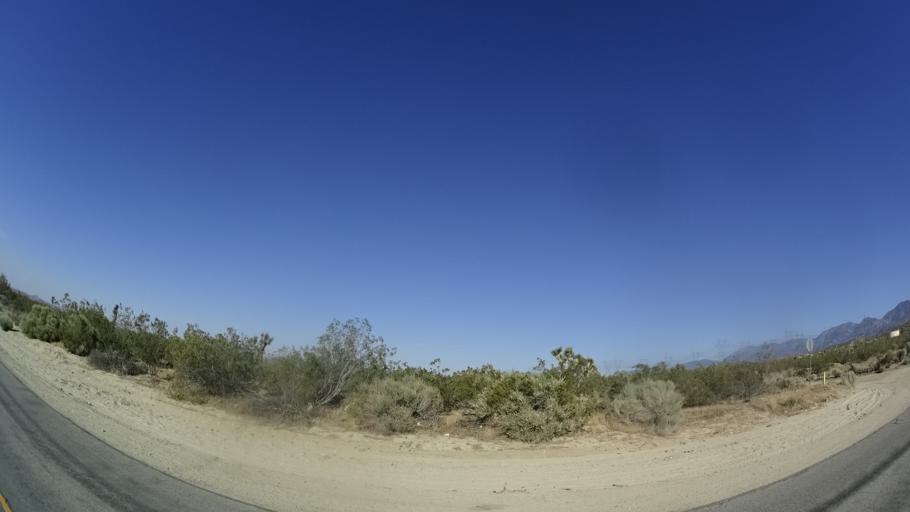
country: US
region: California
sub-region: Los Angeles County
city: Littlerock
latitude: 34.5143
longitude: -117.9749
